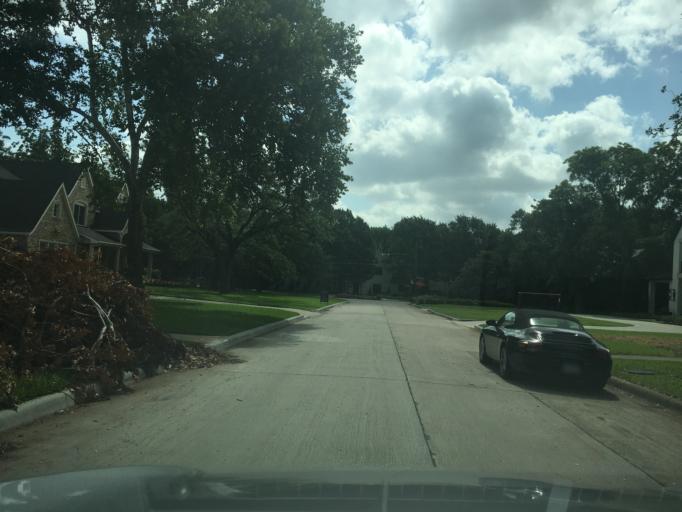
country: US
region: Texas
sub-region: Dallas County
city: Addison
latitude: 32.9107
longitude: -96.8235
